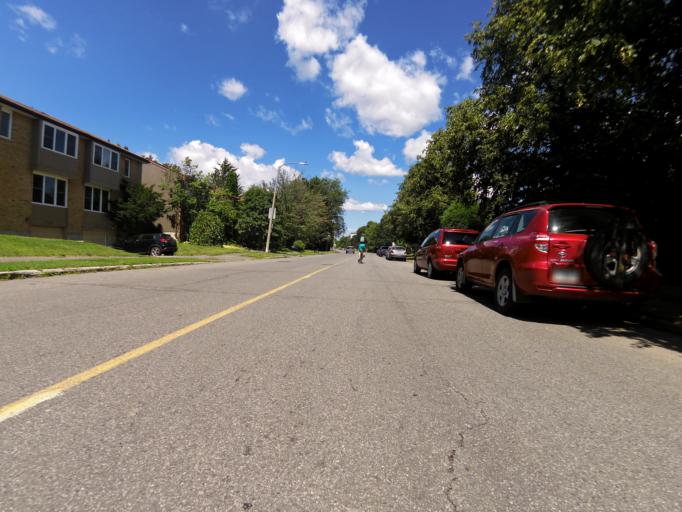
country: CA
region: Ontario
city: Ottawa
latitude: 45.3641
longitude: -75.6846
